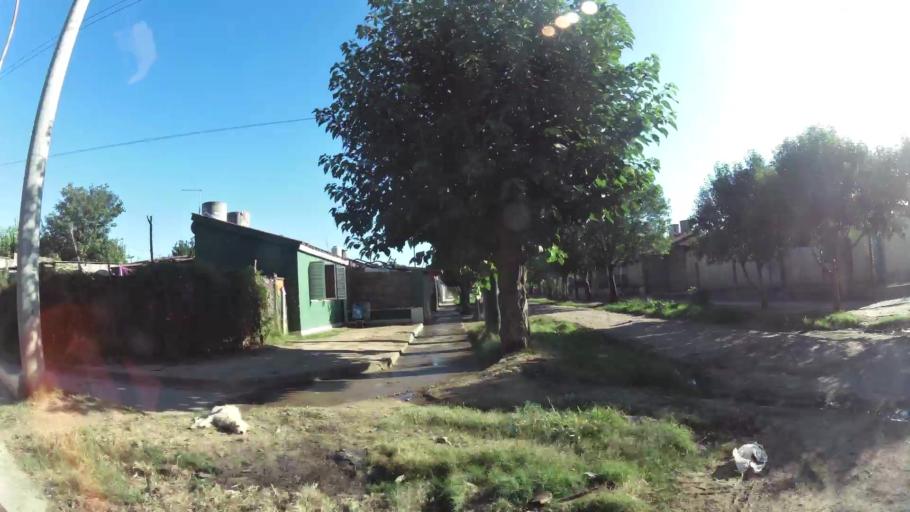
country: AR
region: Cordoba
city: Villa Allende
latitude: -31.3338
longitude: -64.2441
